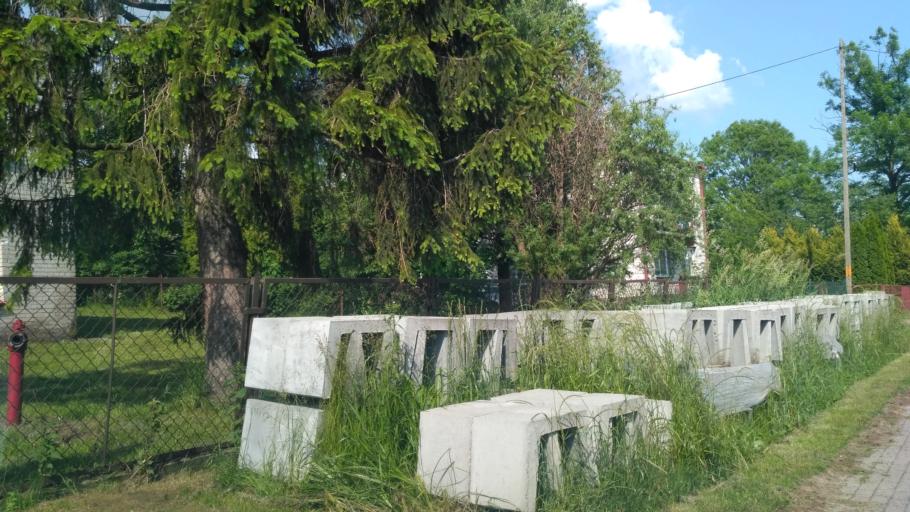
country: PL
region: Subcarpathian Voivodeship
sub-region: Powiat jaroslawski
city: Ostrow
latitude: 49.9387
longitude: 22.7135
